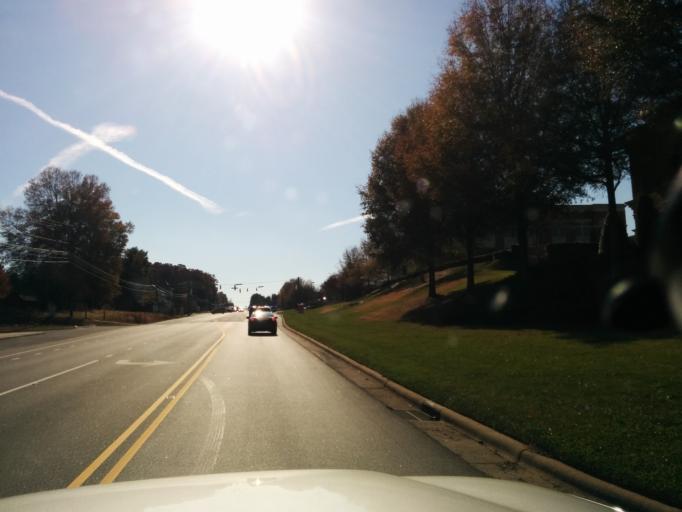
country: US
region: North Carolina
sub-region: Iredell County
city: Mooresville
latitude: 35.5564
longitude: -80.8533
